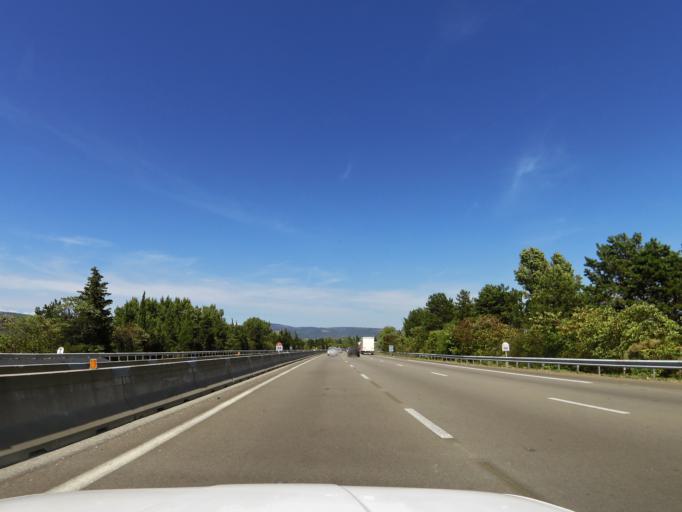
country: FR
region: Rhone-Alpes
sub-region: Departement de la Drome
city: Loriol-sur-Drome
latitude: 44.7427
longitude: 4.7891
